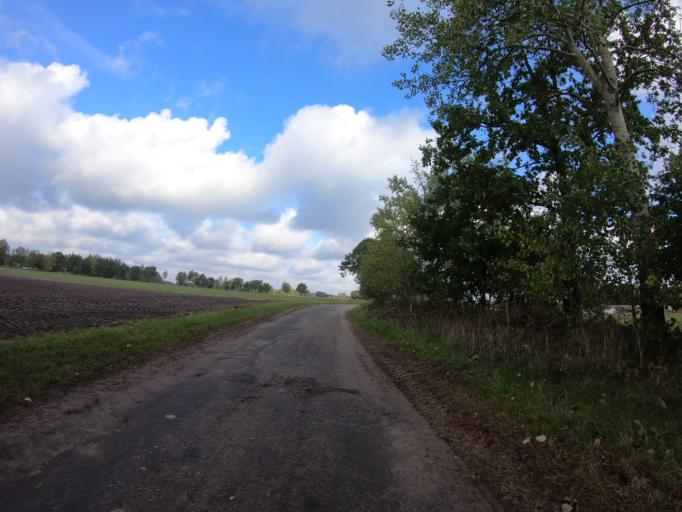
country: DE
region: Lower Saxony
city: Wagenhoff
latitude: 52.5285
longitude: 10.5373
